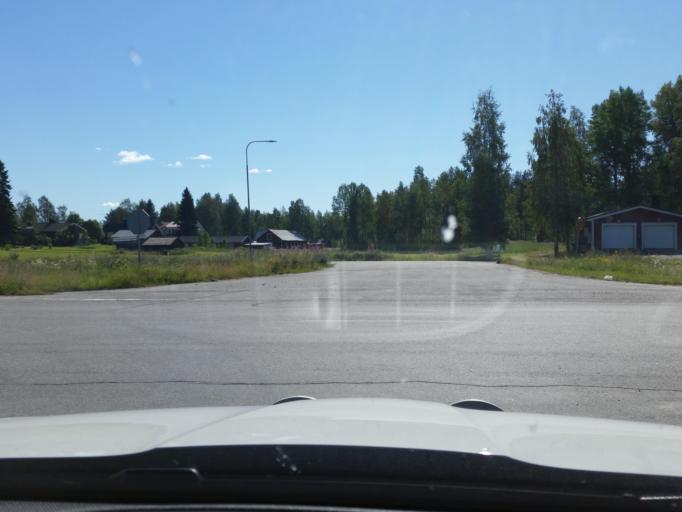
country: SE
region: Norrbotten
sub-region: Pitea Kommun
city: Roknas
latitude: 65.3388
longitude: 21.2308
